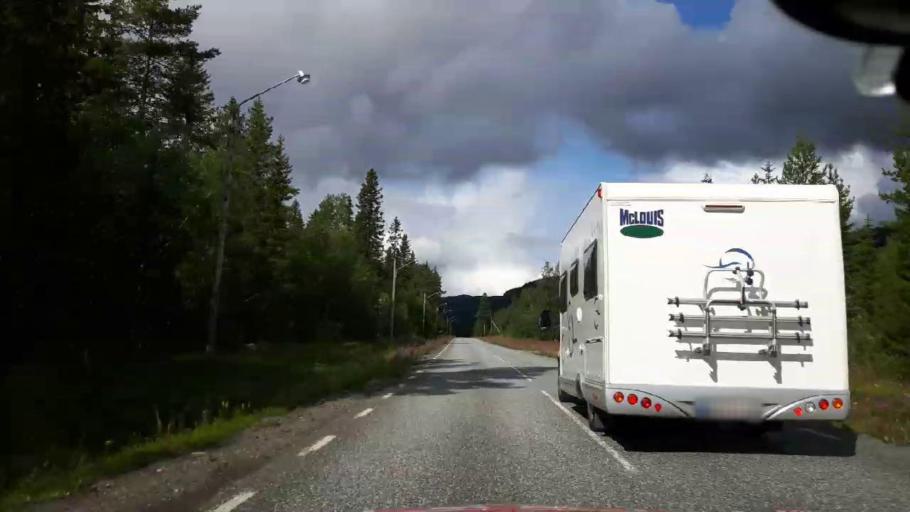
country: SE
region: Vaesterbotten
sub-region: Vilhelmina Kommun
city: Sjoberg
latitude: 64.9404
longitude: 15.8496
